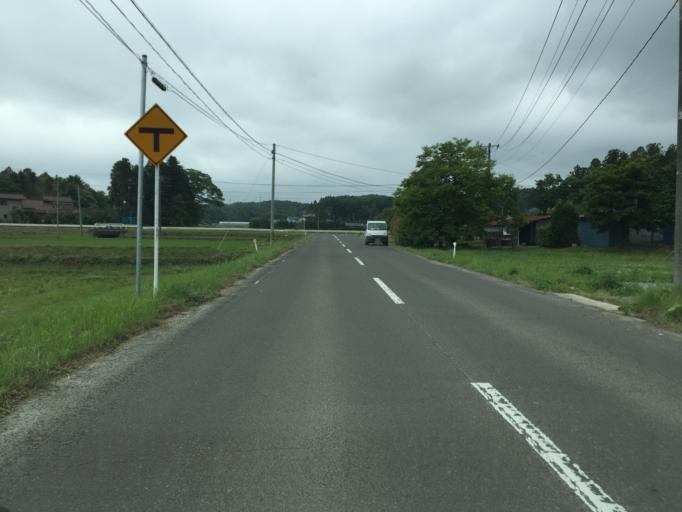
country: JP
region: Miyagi
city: Marumori
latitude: 37.7740
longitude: 140.8954
